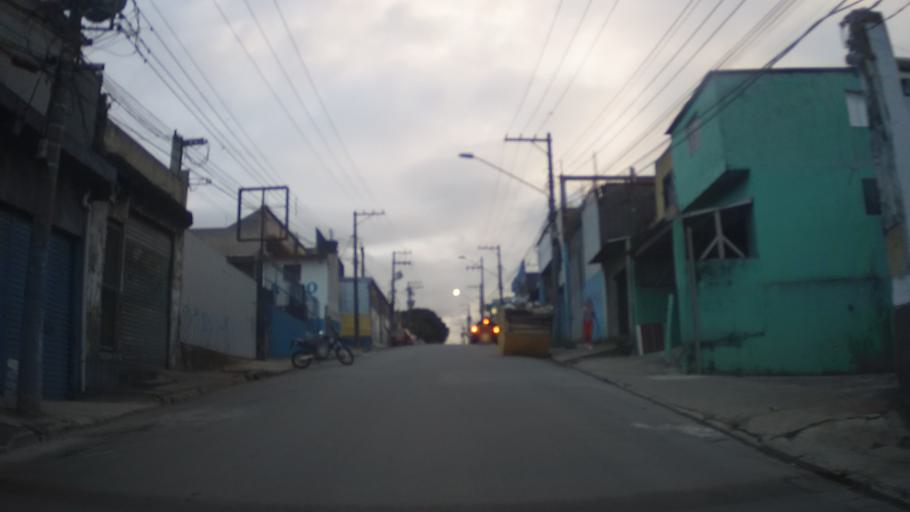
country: BR
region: Sao Paulo
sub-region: Guarulhos
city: Guarulhos
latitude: -23.4618
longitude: -46.4663
